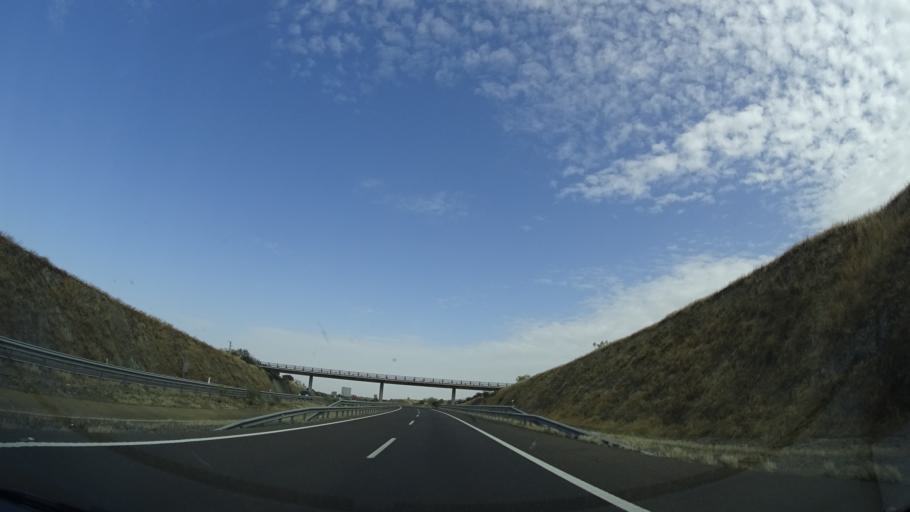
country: ES
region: Extremadura
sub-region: Provincia de Badajoz
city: Fuente de Cantos
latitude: 38.2401
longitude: -6.2904
